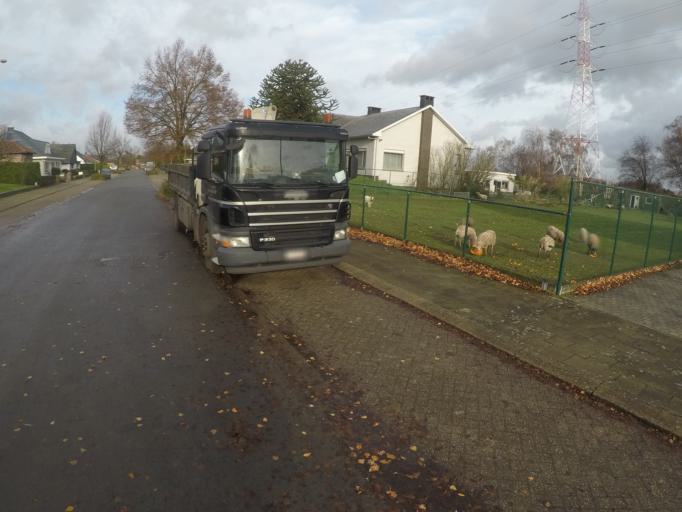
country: BE
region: Flanders
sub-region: Provincie Antwerpen
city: Borsbeek
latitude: 51.1971
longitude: 4.5024
